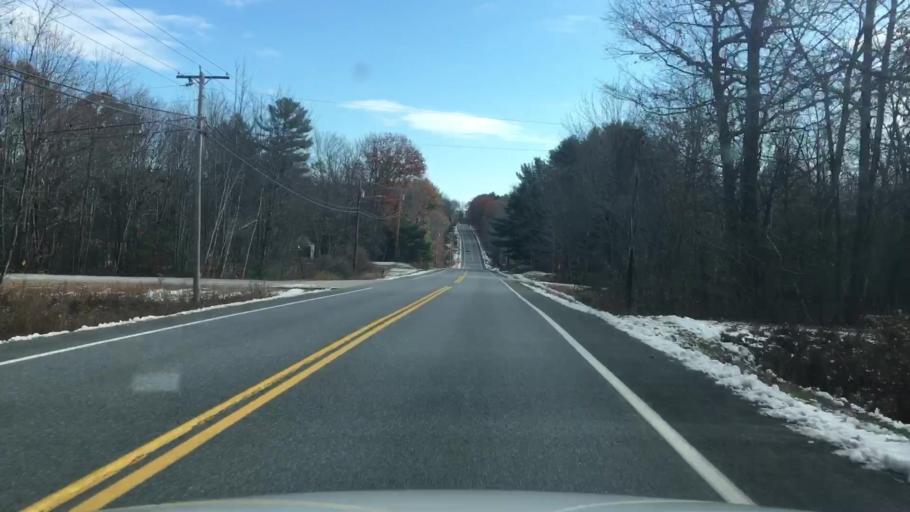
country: US
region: Maine
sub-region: Kennebec County
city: Winthrop
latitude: 44.3257
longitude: -69.9905
